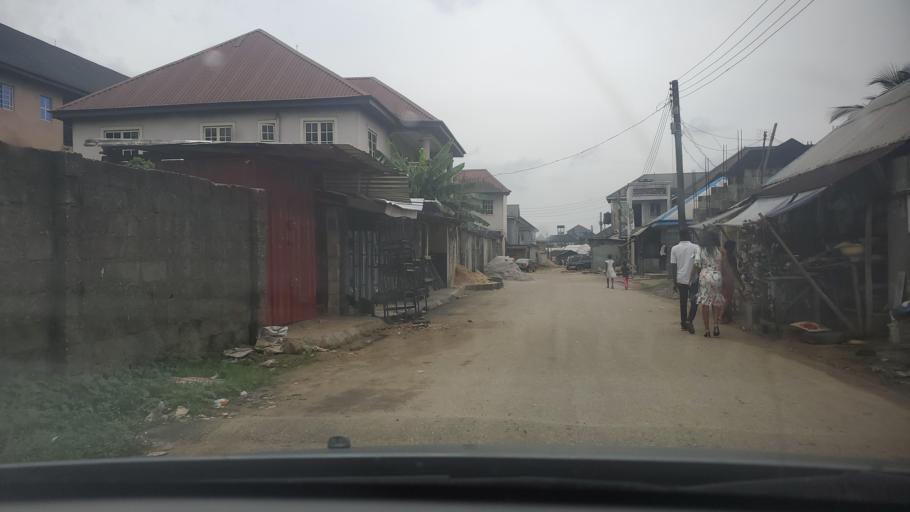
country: NG
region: Rivers
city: Port Harcourt
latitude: 4.8435
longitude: 7.0001
